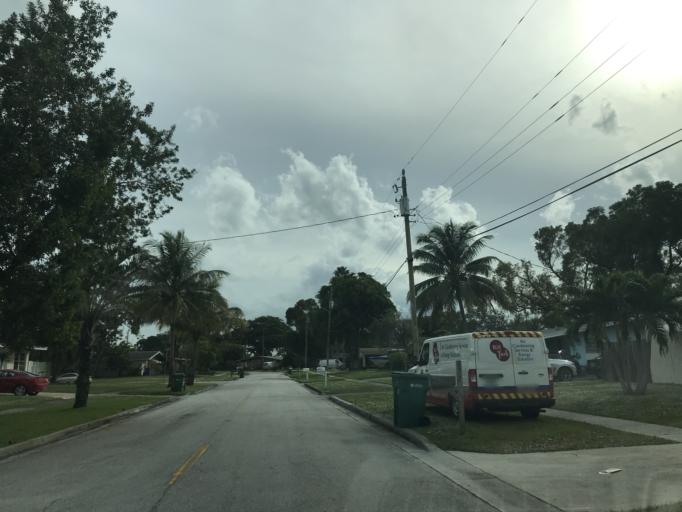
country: US
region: Florida
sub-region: Broward County
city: Margate
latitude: 26.2571
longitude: -80.2037
